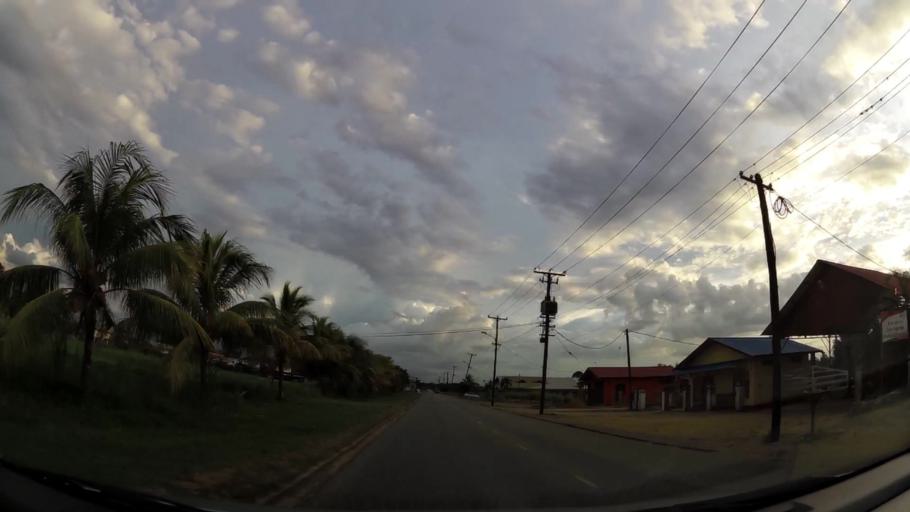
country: SR
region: Paramaribo
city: Paramaribo
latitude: 5.7805
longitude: -55.1670
